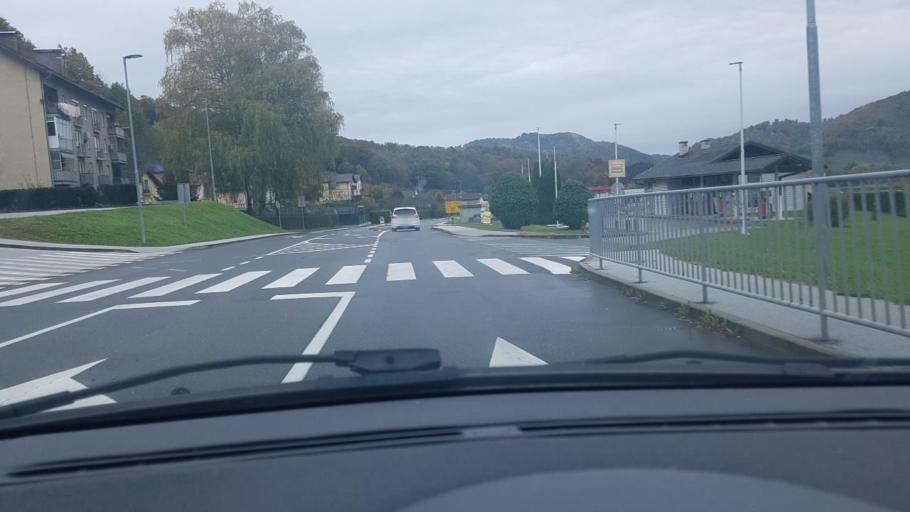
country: SI
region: Majsperk
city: Majsperk
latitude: 46.3503
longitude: 15.7359
